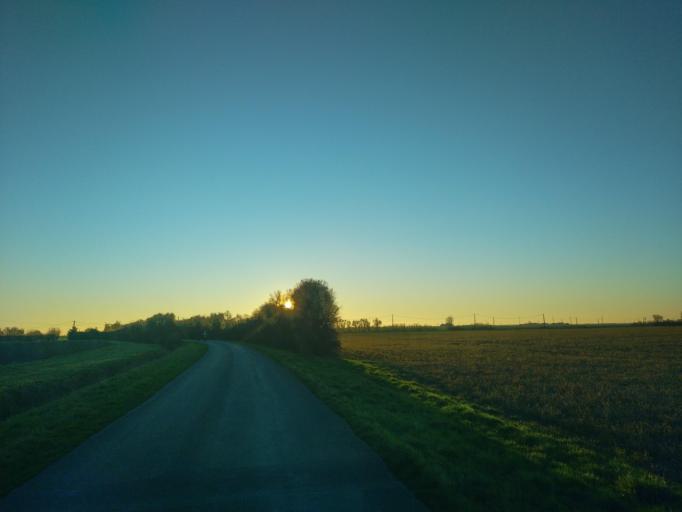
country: FR
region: Pays de la Loire
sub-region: Departement de la Vendee
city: Triaize
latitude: 46.3756
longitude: -1.2987
